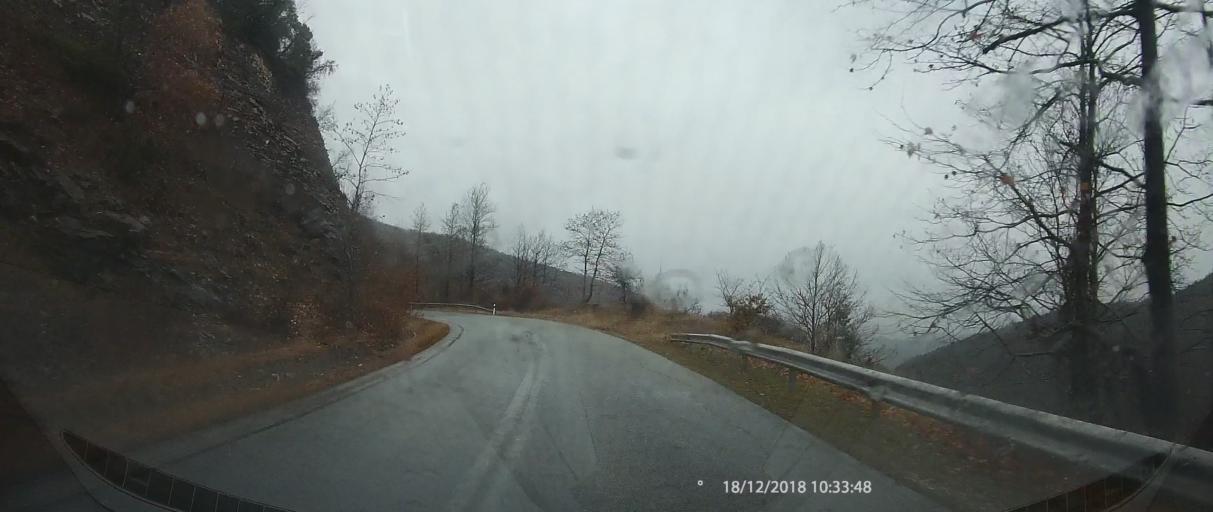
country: GR
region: Central Macedonia
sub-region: Nomos Pierias
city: Kato Milia
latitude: 40.2010
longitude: 22.3010
